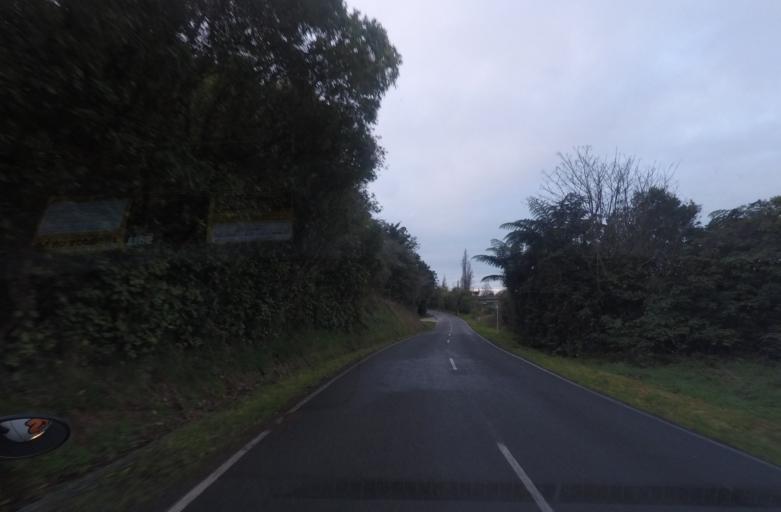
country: NZ
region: Tasman
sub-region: Tasman District
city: Takaka
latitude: -40.8309
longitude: 172.7907
